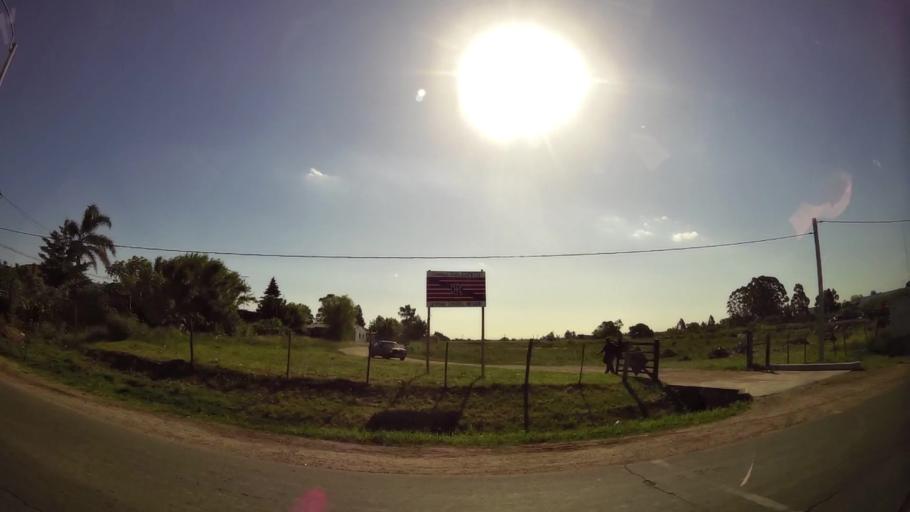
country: UY
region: Canelones
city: La Paz
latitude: -34.8164
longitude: -56.1577
